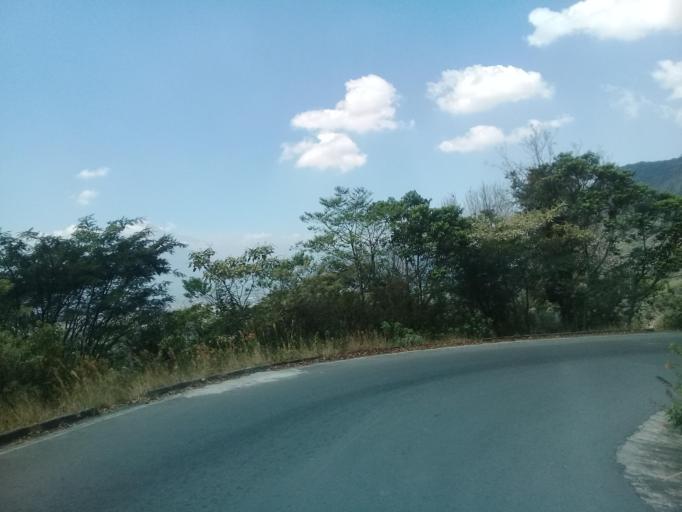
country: MX
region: Veracruz
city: Jalapilla
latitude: 18.8124
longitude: -97.0616
